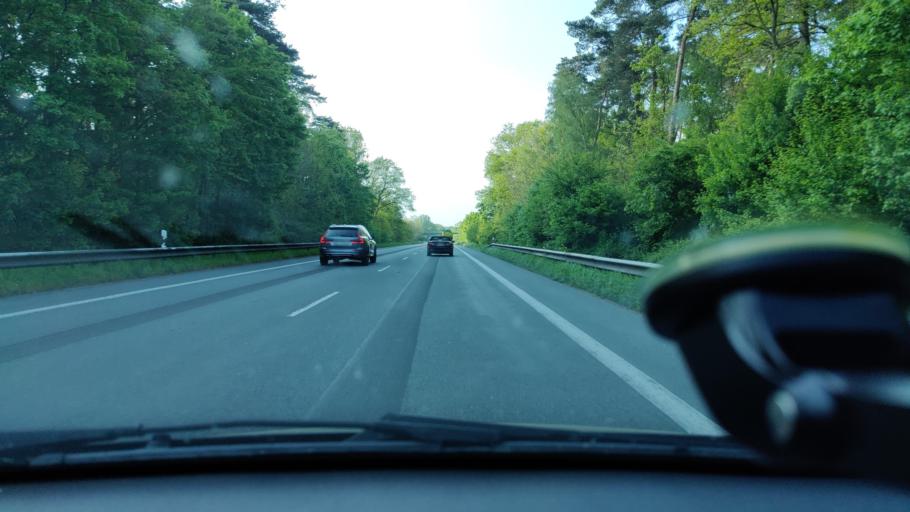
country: DE
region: North Rhine-Westphalia
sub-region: Regierungsbezirk Munster
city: Telgte
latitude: 51.9762
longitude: 7.8182
